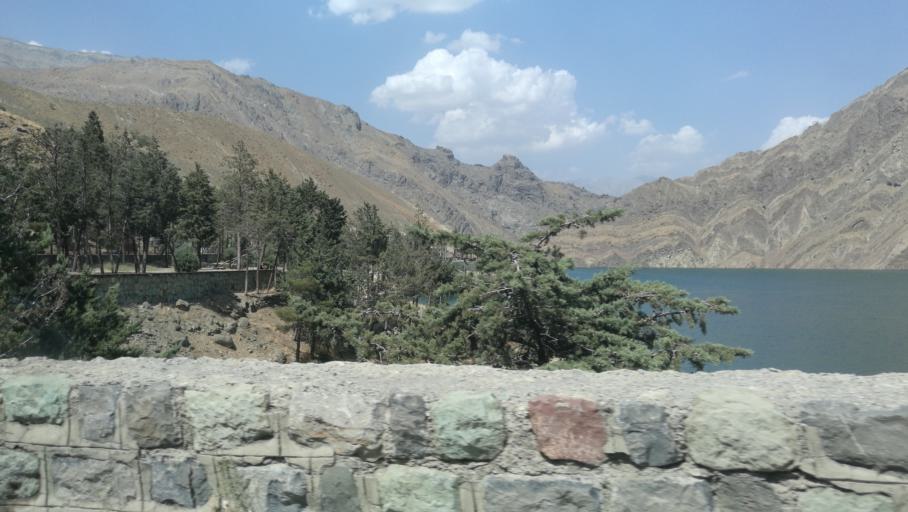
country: IR
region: Alborz
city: Karaj
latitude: 35.9689
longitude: 51.0937
